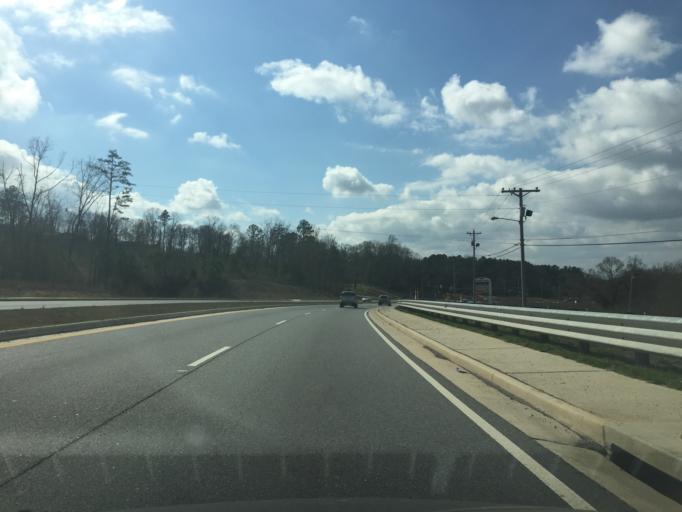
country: US
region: Georgia
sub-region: Catoosa County
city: Indian Springs
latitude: 34.9615
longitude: -85.1952
